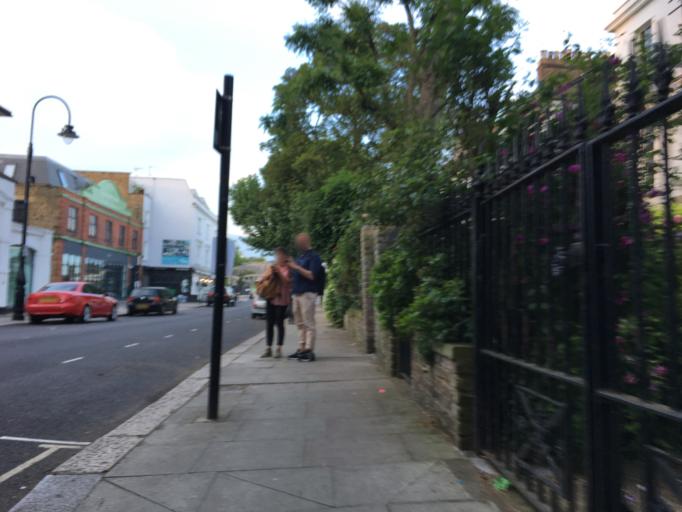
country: GB
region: England
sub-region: Greater London
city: Camden Town
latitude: 51.5421
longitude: -0.1562
